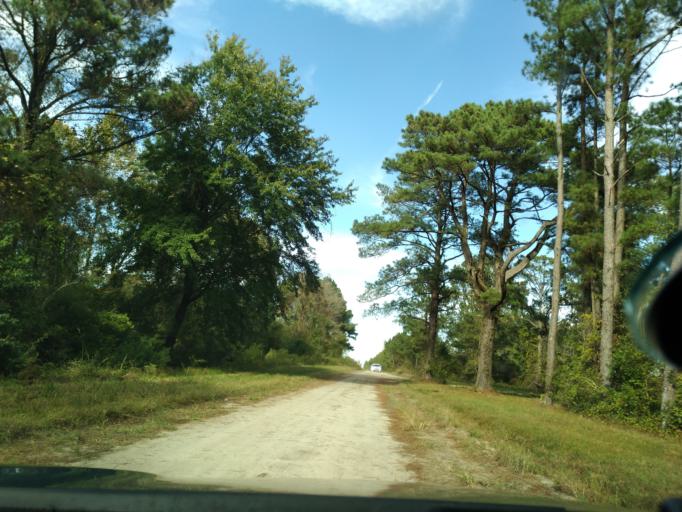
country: US
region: North Carolina
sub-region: Beaufort County
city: Belhaven
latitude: 35.7291
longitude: -76.5754
